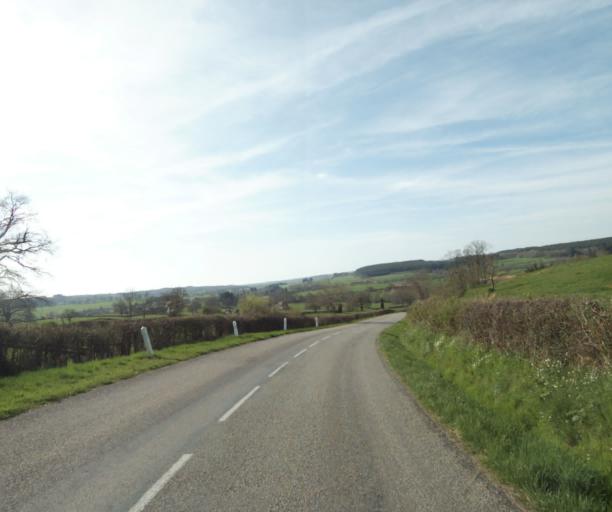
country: FR
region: Bourgogne
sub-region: Departement de Saone-et-Loire
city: Charolles
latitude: 46.4313
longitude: 4.4182
